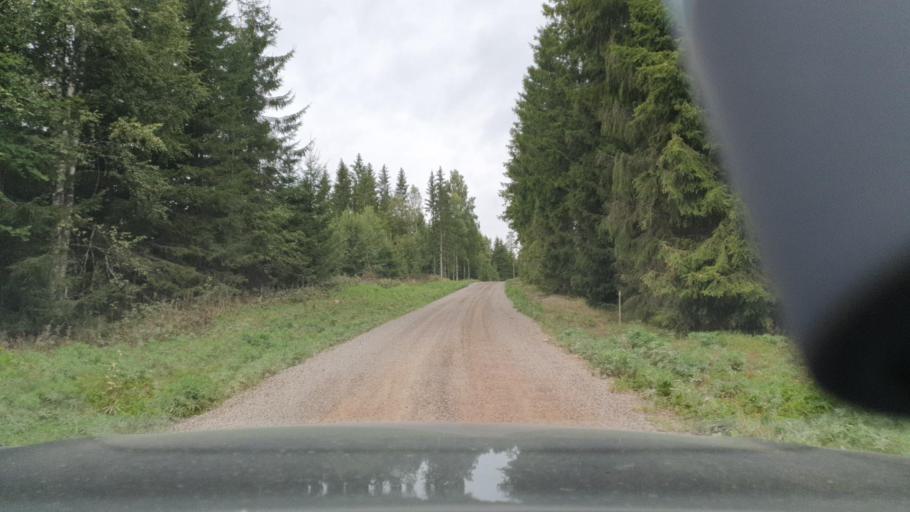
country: SE
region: Vaermland
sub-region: Torsby Kommun
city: Torsby
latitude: 59.9411
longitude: 12.8048
